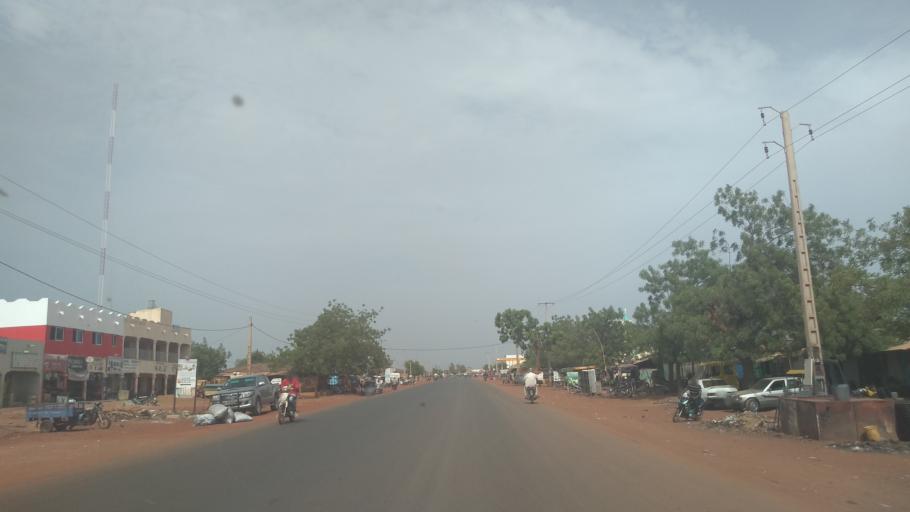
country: ML
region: Bamako
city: Bamako
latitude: 12.5876
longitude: -7.8362
